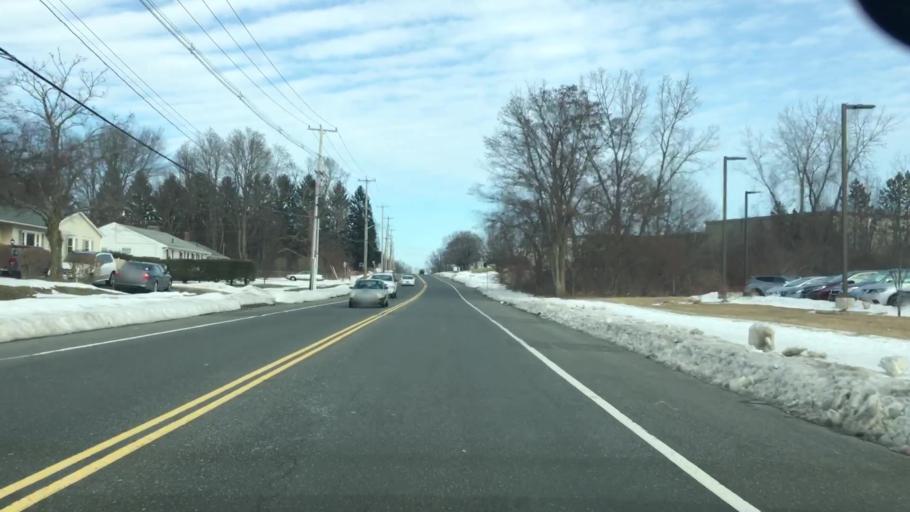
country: US
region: Massachusetts
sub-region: Hampden County
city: Holyoke
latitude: 42.1825
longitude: -72.6378
